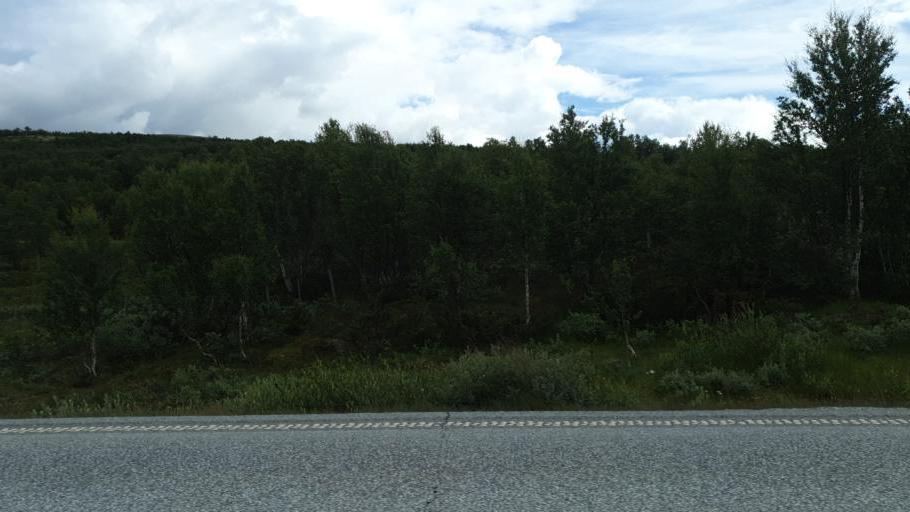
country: NO
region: Oppland
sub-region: Dovre
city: Dovre
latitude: 62.1081
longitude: 9.2688
